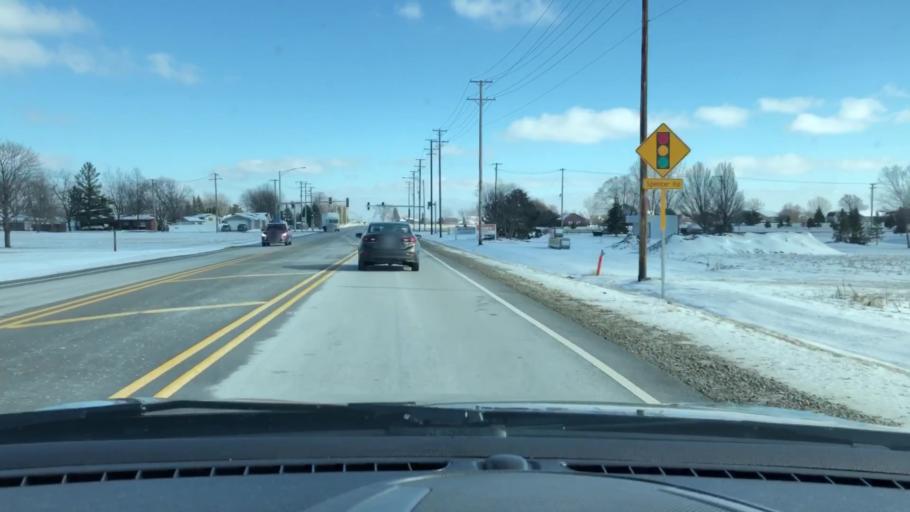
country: US
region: Illinois
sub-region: Will County
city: New Lenox
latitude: 41.4834
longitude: -87.9429
